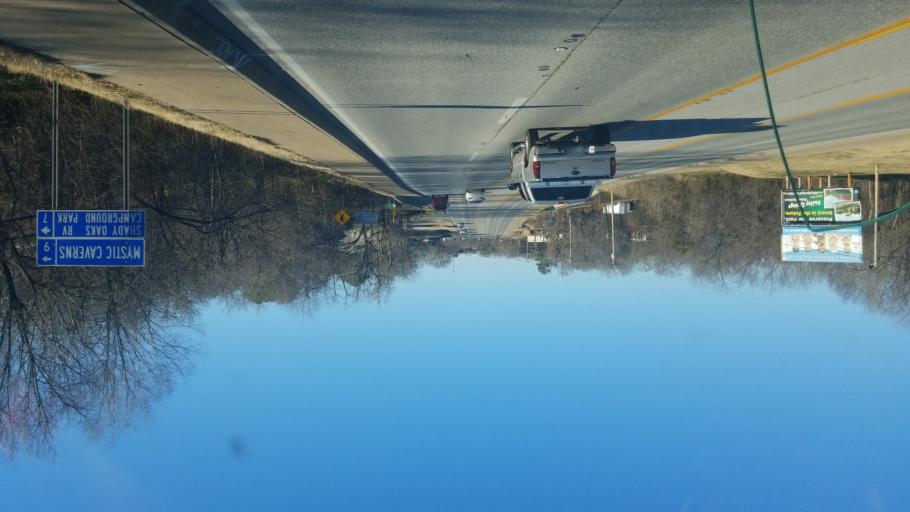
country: US
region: Arkansas
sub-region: Boone County
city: Harrison
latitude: 36.2013
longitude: -93.0502
